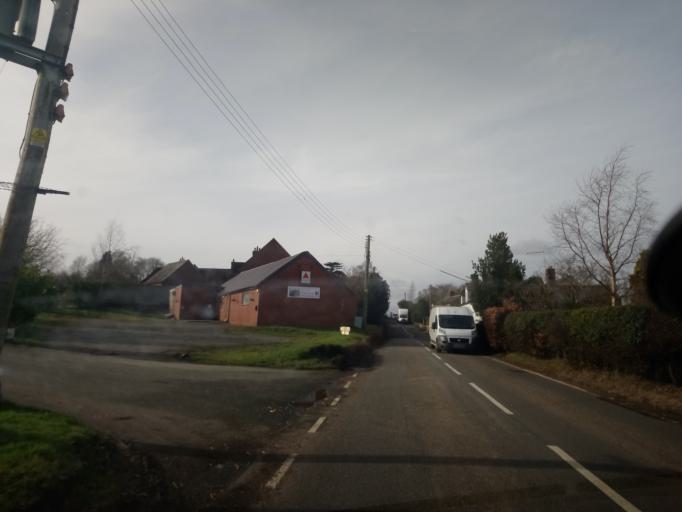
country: GB
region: England
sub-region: Shropshire
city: Stoke upon Tern
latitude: 52.8611
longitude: -2.5984
